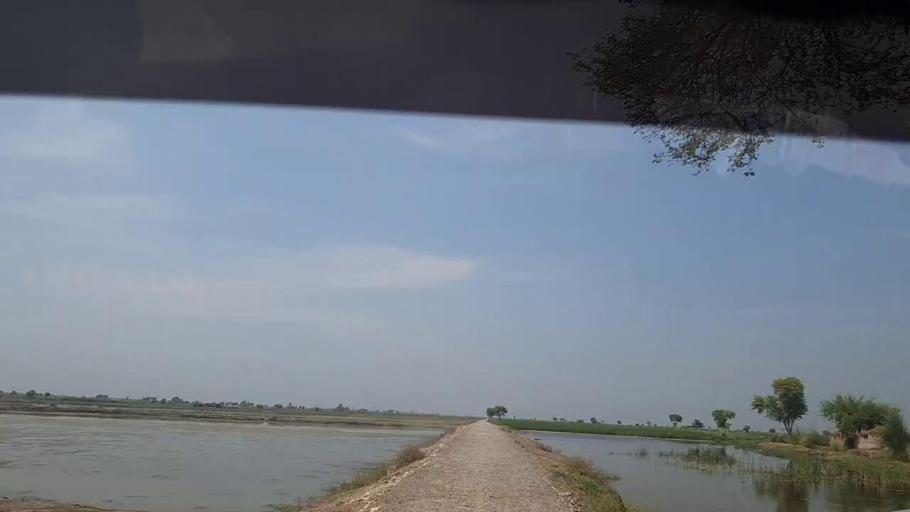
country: PK
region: Sindh
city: Thul
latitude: 28.2097
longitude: 68.6887
